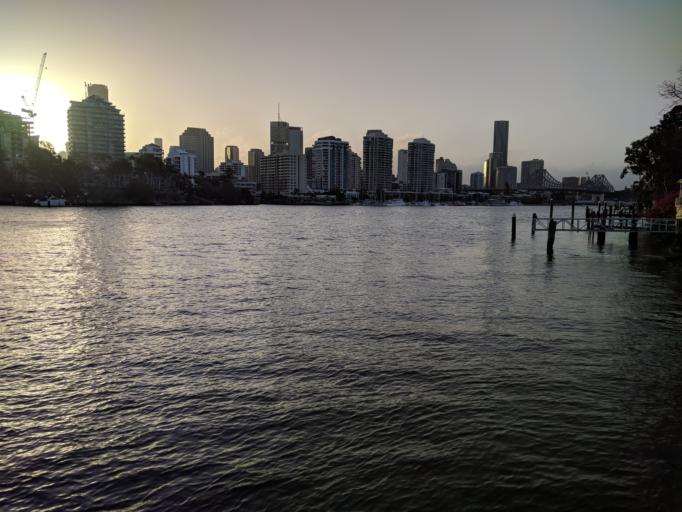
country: AU
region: Queensland
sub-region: Brisbane
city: Woolloongabba
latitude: -27.4746
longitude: 153.0425
